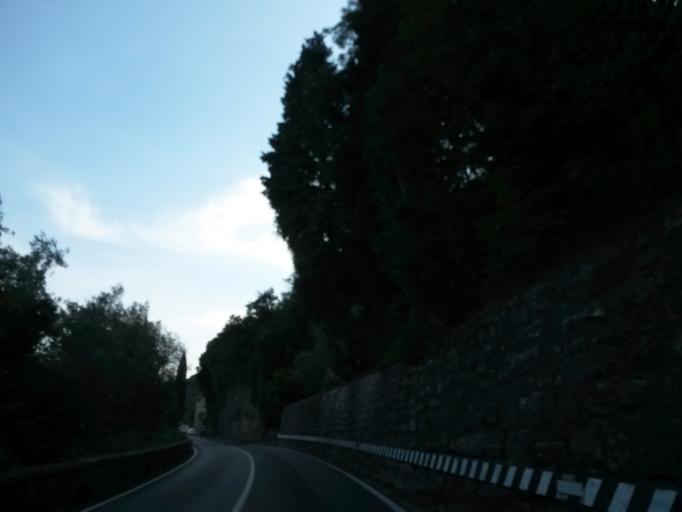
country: IT
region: Lombardy
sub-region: Provincia di Brescia
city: Gardola
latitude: 45.7169
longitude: 10.7042
